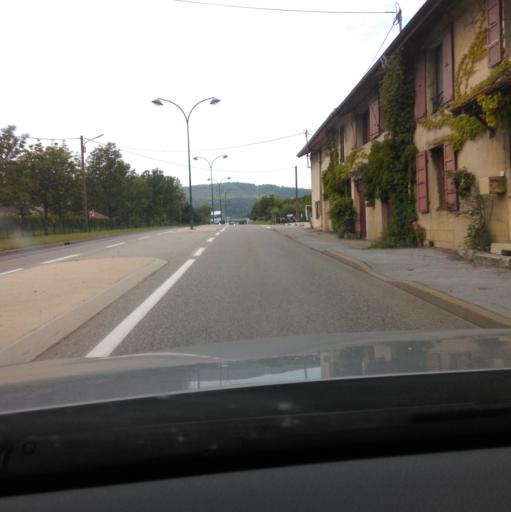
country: FR
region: Rhone-Alpes
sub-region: Departement de l'Ain
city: Montreal-la-Cluse
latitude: 46.1775
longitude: 5.5553
